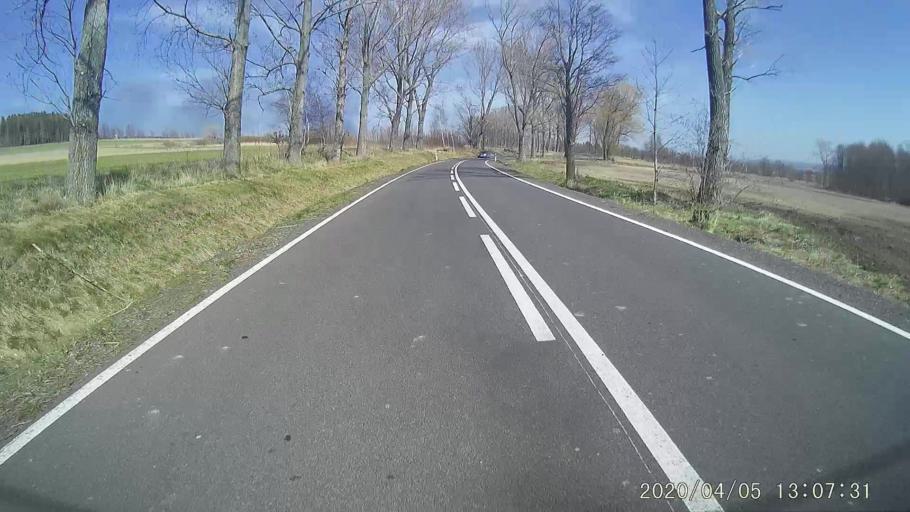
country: PL
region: Lower Silesian Voivodeship
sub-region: Powiat lubanski
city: Lesna
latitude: 50.9825
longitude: 15.3149
